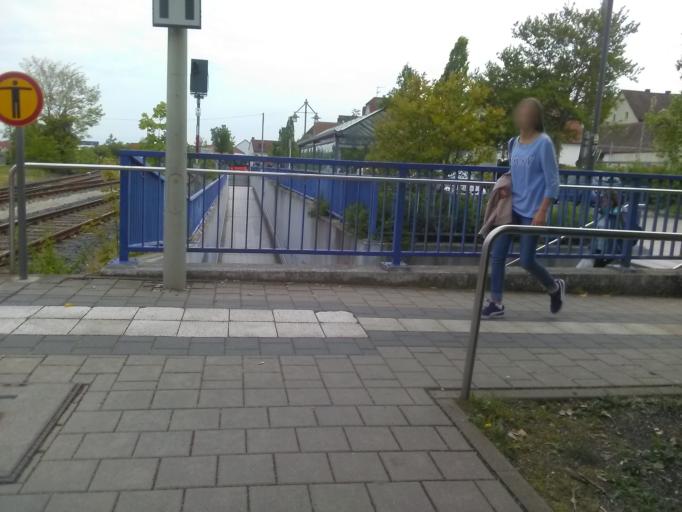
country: DE
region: Bavaria
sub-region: Upper Franconia
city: Kleinsendelbach
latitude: 49.5754
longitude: 11.1990
